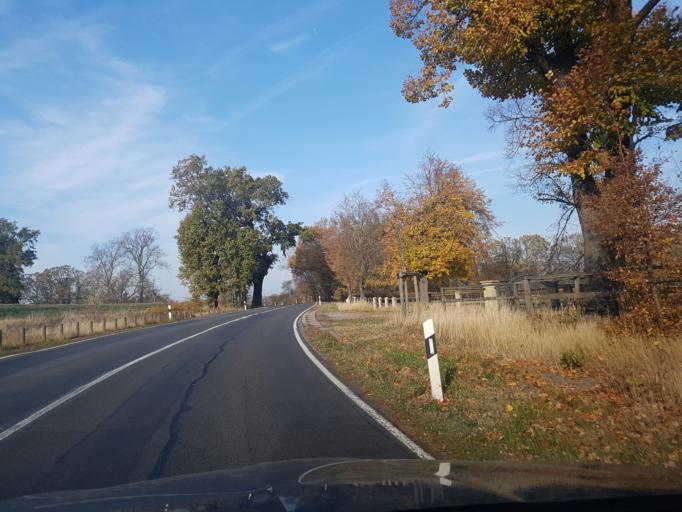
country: DE
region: Saxony
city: Beilrode
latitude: 51.5481
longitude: 13.0496
